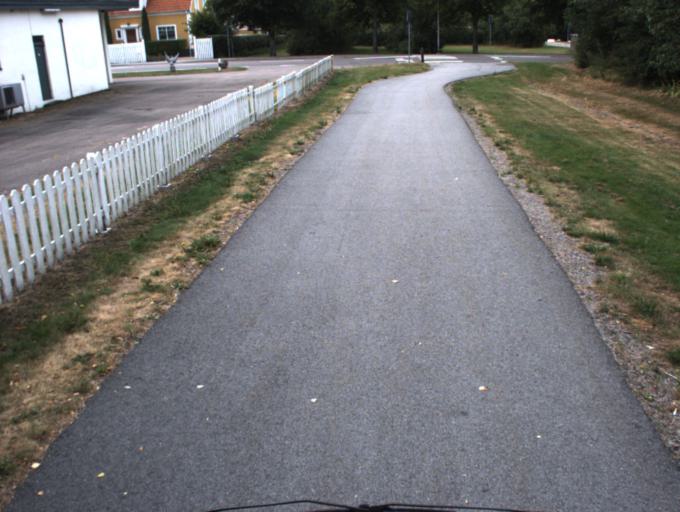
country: SE
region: Skane
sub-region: Helsingborg
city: Morarp
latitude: 56.0573
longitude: 12.8808
